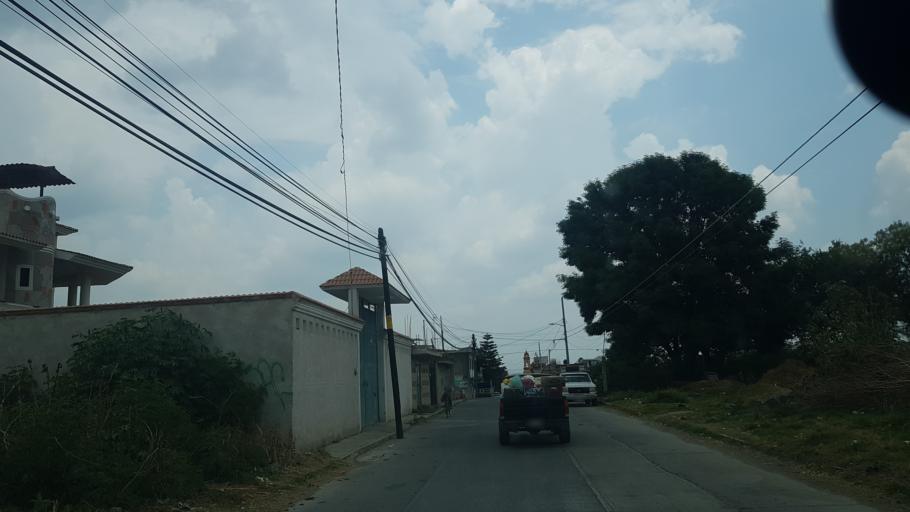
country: MX
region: Puebla
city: Huejotzingo
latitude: 19.1619
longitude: -98.4135
